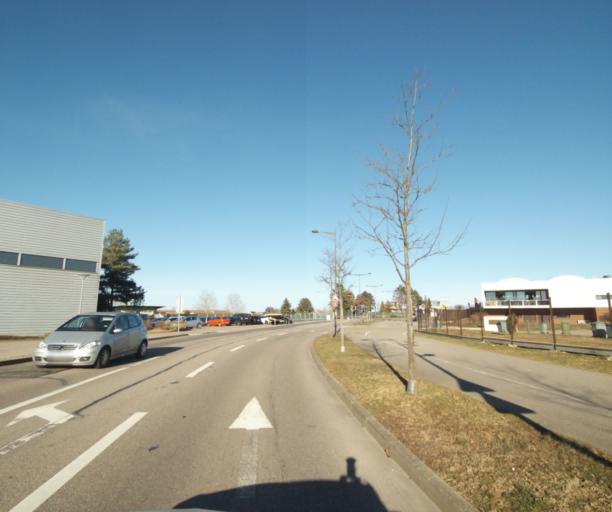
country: FR
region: Lorraine
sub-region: Departement de Meurthe-et-Moselle
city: Heillecourt
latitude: 48.6569
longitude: 6.2073
